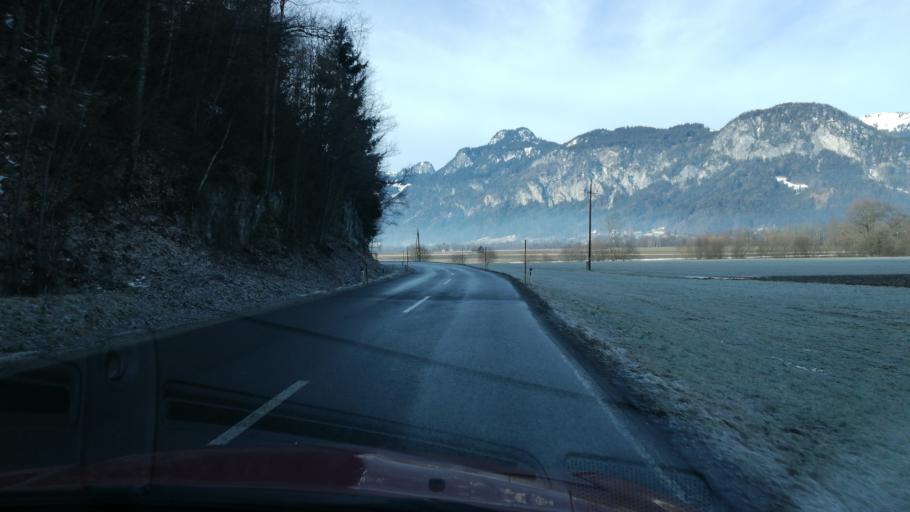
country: AT
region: Styria
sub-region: Politischer Bezirk Liezen
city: Worschach
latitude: 47.5416
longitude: 14.1689
